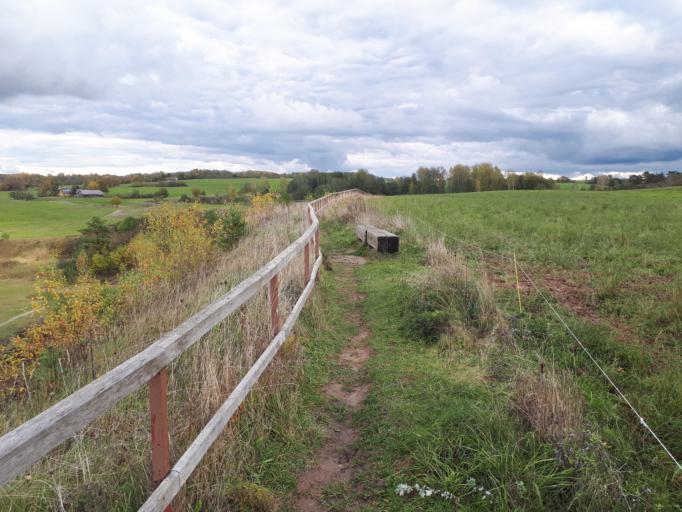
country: LT
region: Utenos apskritis
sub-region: Utena
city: Utena
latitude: 55.6525
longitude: 25.5953
